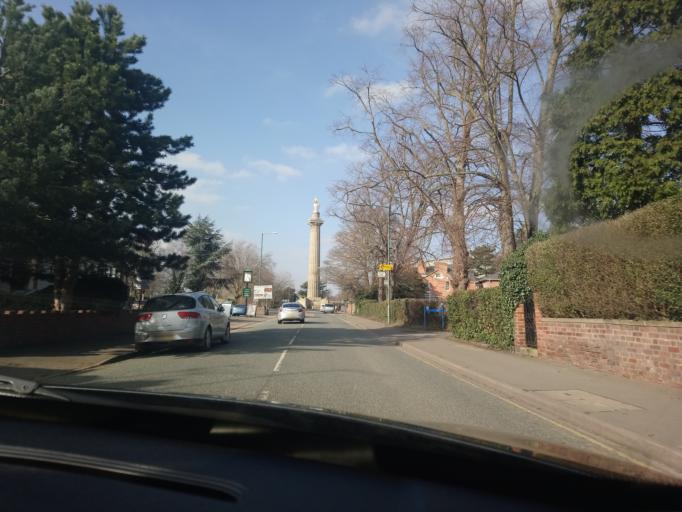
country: GB
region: England
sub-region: Shropshire
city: Shrewsbury
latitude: 52.7028
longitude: -2.7304
